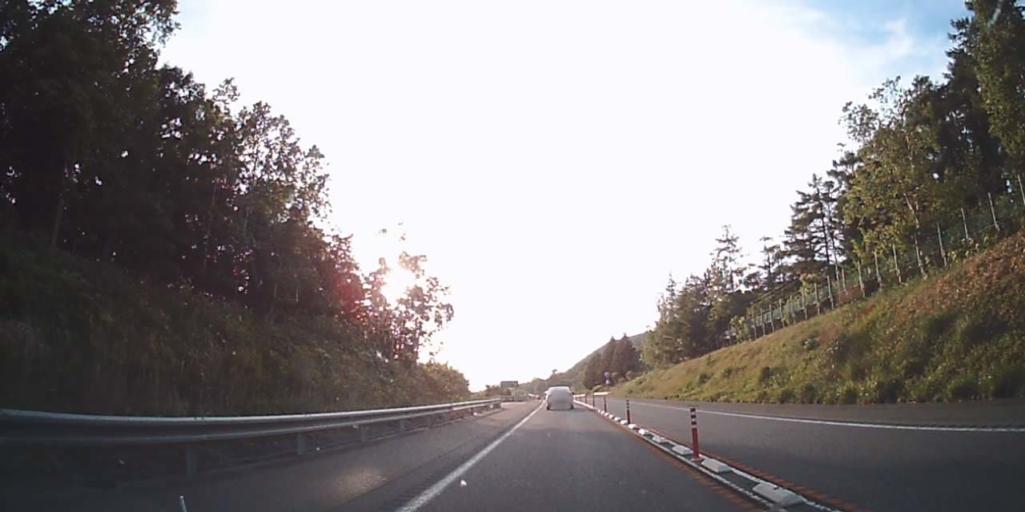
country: JP
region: Hokkaido
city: Date
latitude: 42.5138
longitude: 140.8322
